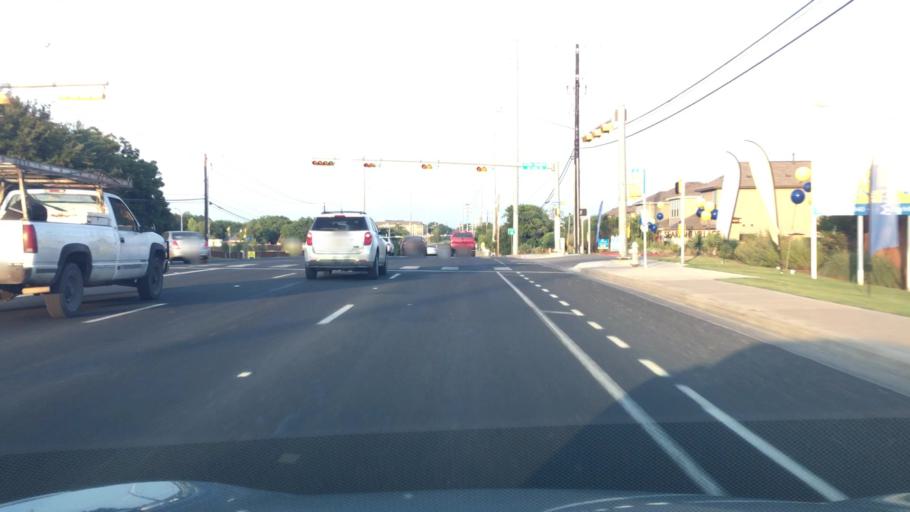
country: US
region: Texas
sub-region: Travis County
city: Manchaca
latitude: 30.1738
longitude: -97.8096
